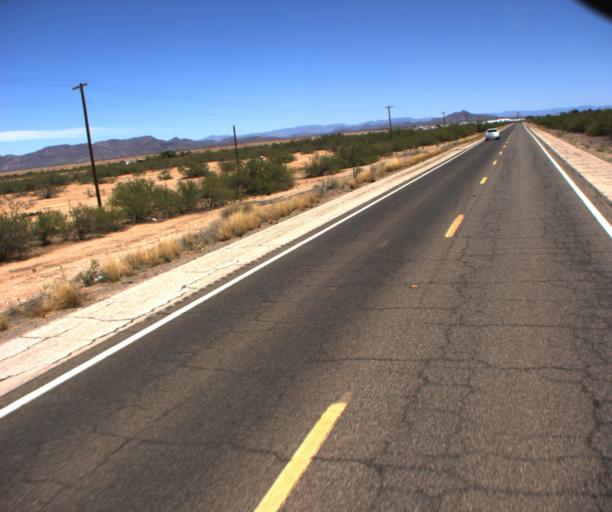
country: US
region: Arizona
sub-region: Yavapai County
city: Congress
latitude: 33.9358
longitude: -113.2033
